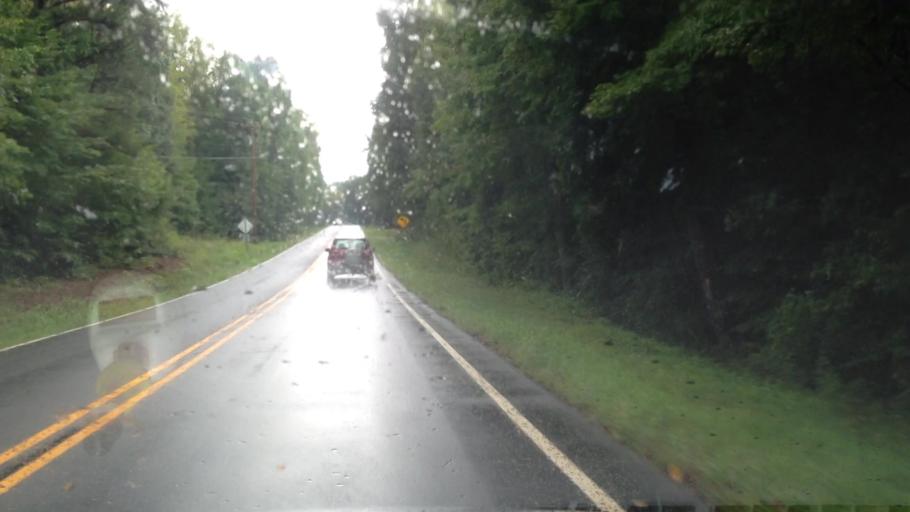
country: US
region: North Carolina
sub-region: Stokes County
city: Walnut Cove
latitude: 36.3857
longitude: -80.0962
